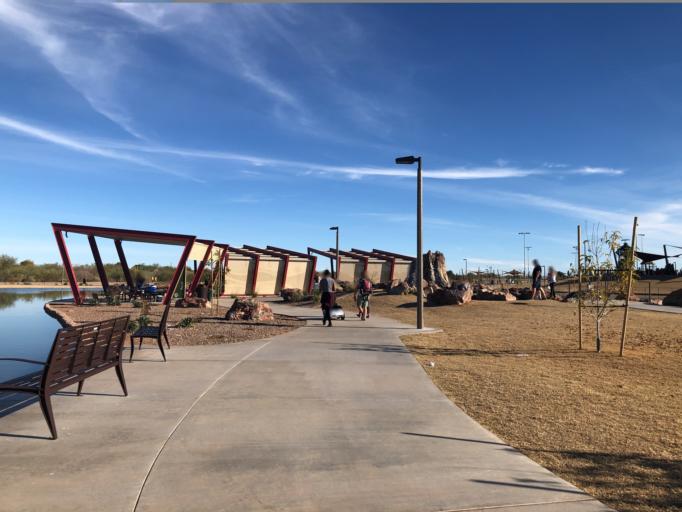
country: US
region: Arizona
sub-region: Maricopa County
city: Queen Creek
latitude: 33.2558
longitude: -111.6598
